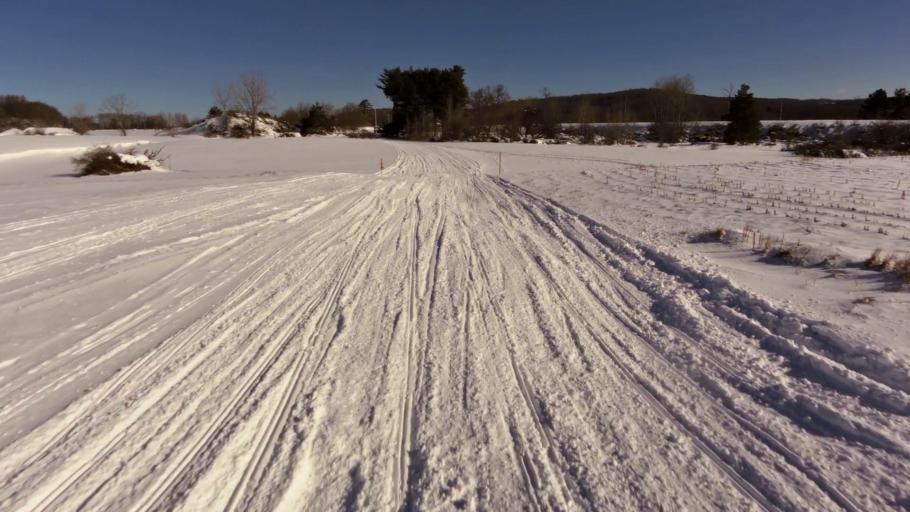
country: US
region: New York
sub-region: Cattaraugus County
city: Franklinville
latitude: 42.3675
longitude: -78.4649
